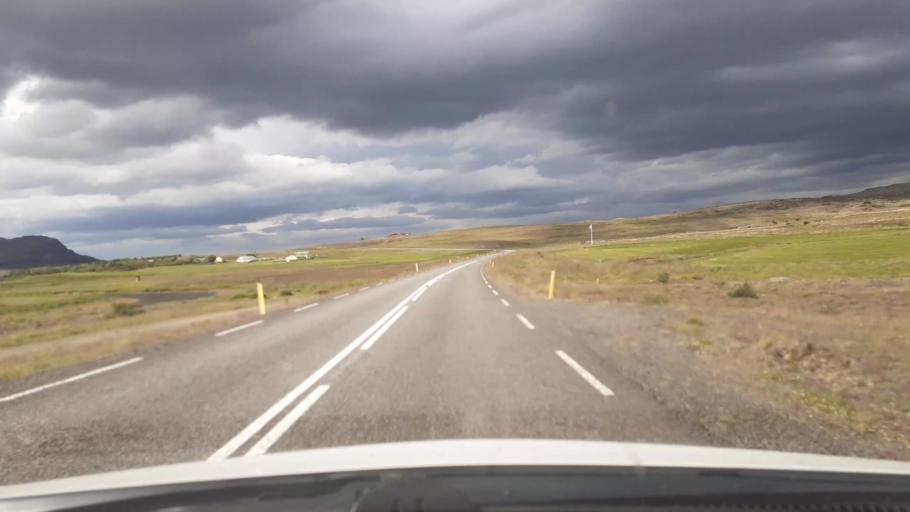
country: IS
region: West
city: Borgarnes
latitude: 64.5450
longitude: -21.6390
